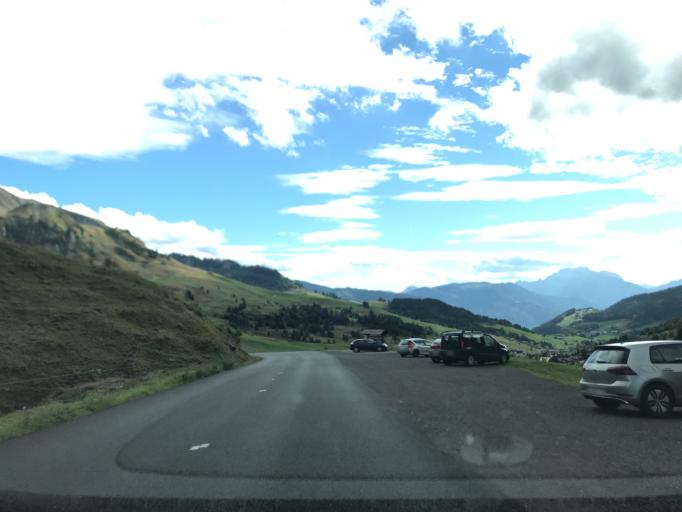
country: FR
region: Rhone-Alpes
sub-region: Departement de la Haute-Savoie
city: Le Grand-Bornand
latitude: 45.9837
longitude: 6.4654
